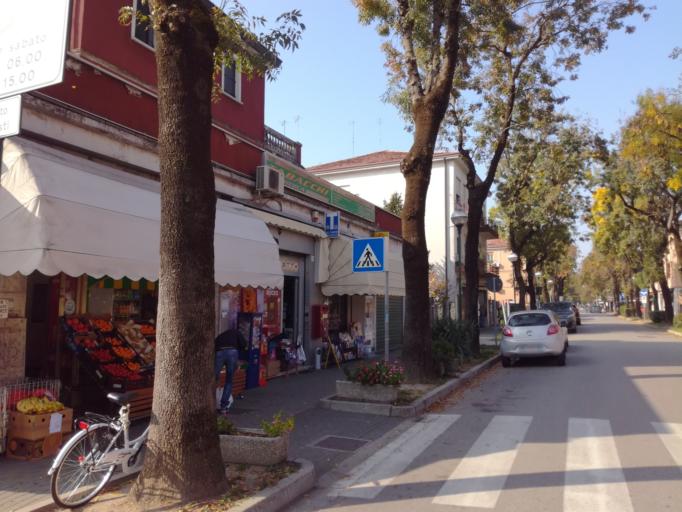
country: IT
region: Veneto
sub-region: Provincia di Venezia
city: Mestre
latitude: 45.4754
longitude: 12.2270
